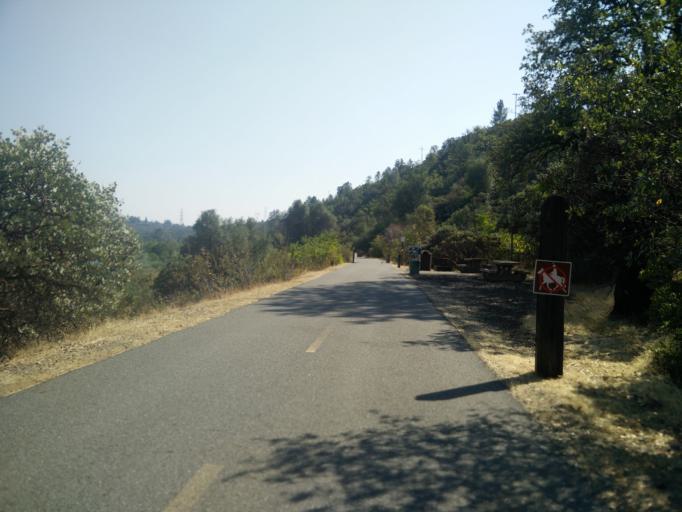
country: US
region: California
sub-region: Shasta County
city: Shasta
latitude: 40.6005
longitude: -122.4444
